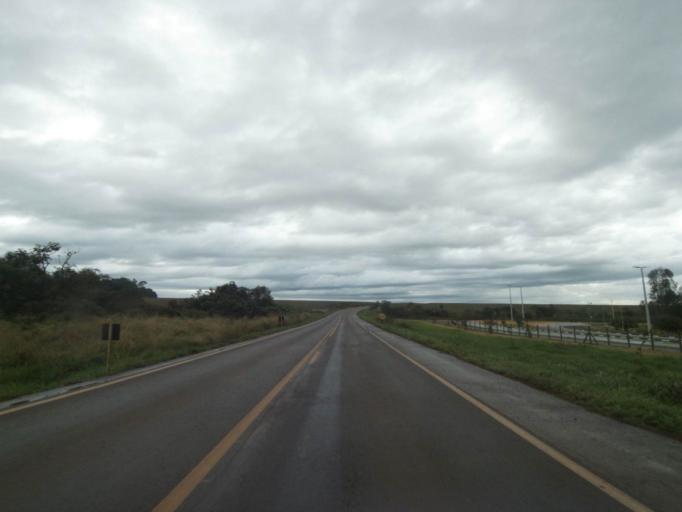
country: BR
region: Parana
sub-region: Toledo
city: Toledo
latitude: -24.6894
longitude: -53.7536
